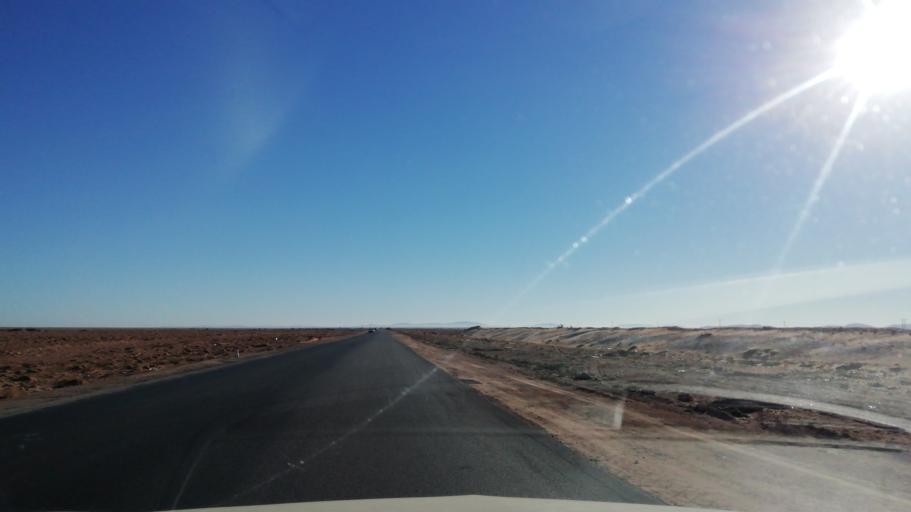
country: DZ
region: El Bayadh
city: El Bayadh
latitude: 33.8583
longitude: 0.5736
